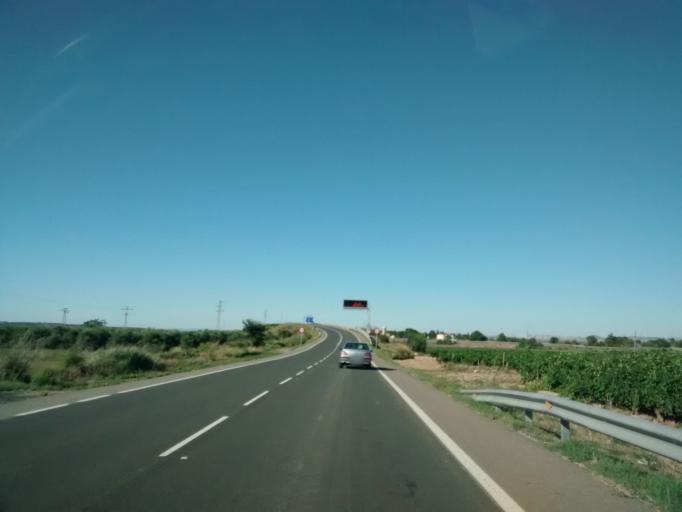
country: ES
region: Navarre
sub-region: Provincia de Navarra
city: Murchante
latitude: 42.0292
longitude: -1.6394
